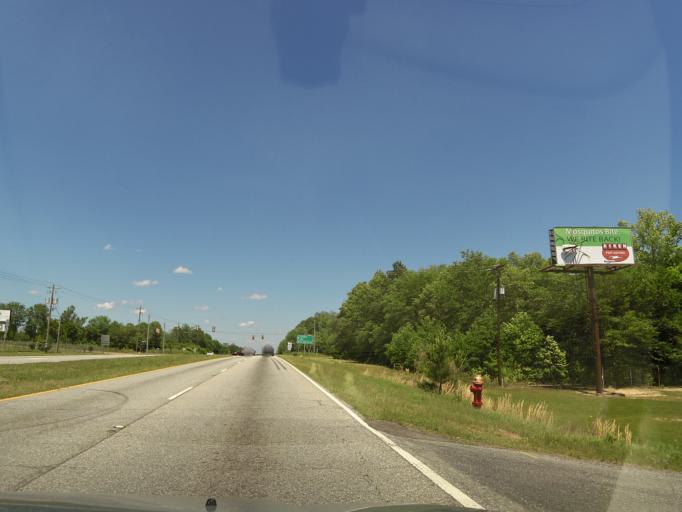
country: US
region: South Carolina
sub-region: Aiken County
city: Clearwater
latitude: 33.4921
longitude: -81.9178
